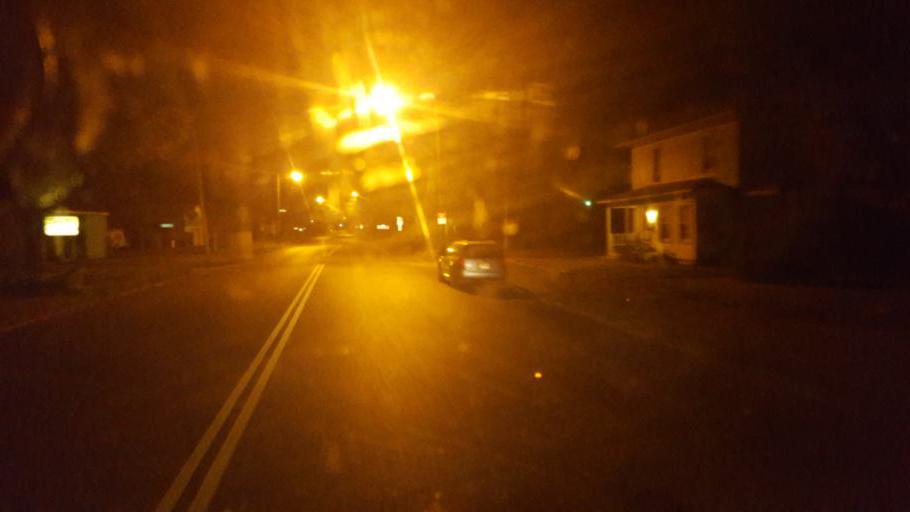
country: US
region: Ohio
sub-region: Knox County
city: Mount Vernon
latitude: 40.4035
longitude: -82.4919
